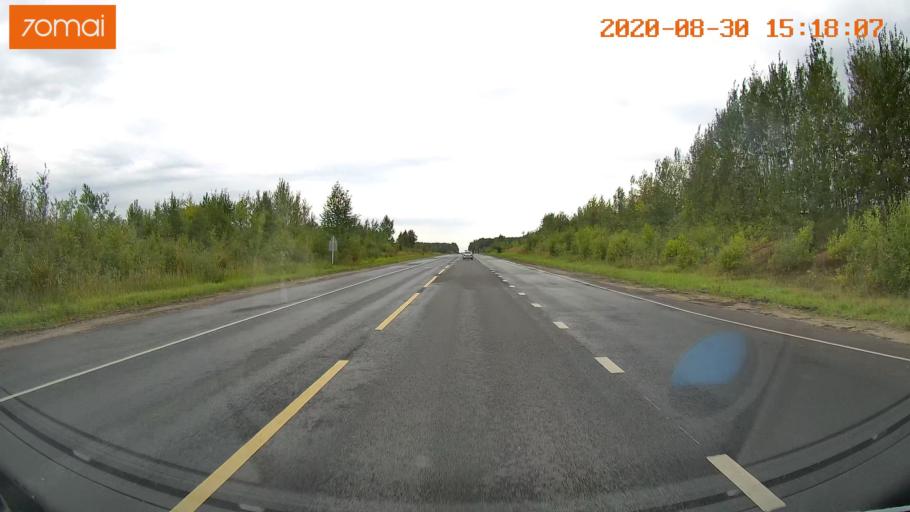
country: RU
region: Ivanovo
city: Rodniki
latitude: 57.1266
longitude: 41.7969
